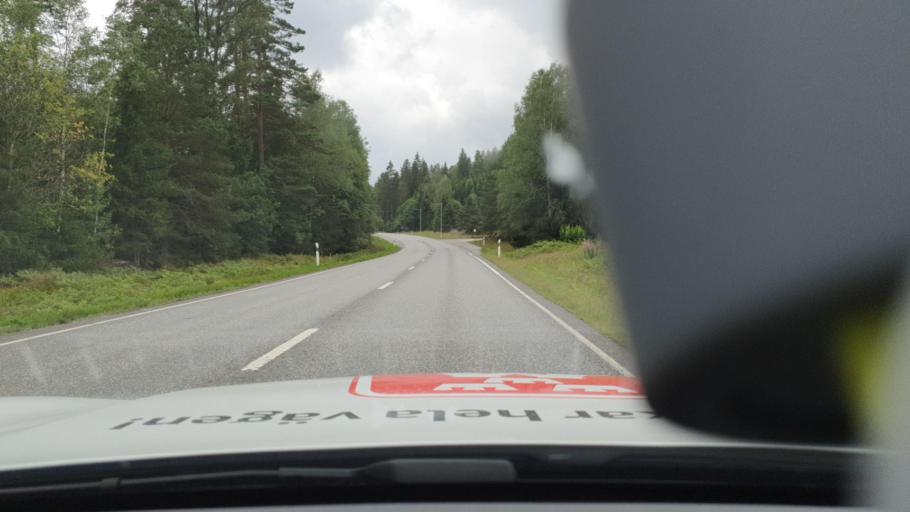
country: SE
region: Joenkoeping
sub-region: Gislaveds Kommun
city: Smalandsstenar
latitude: 57.2078
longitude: 13.4445
